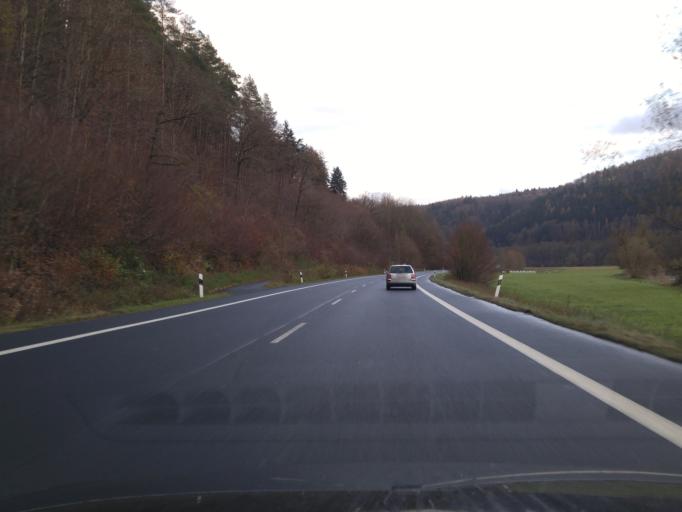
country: DE
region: Lower Saxony
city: Hannoversch Munden
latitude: 51.4142
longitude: 9.6817
